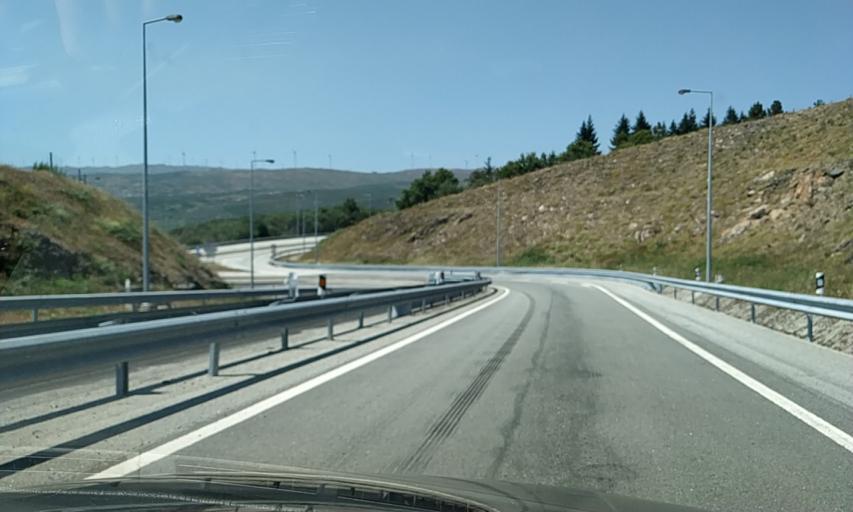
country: PT
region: Viseu
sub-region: Castro Daire
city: Castro Daire
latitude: 40.9382
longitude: -7.9113
